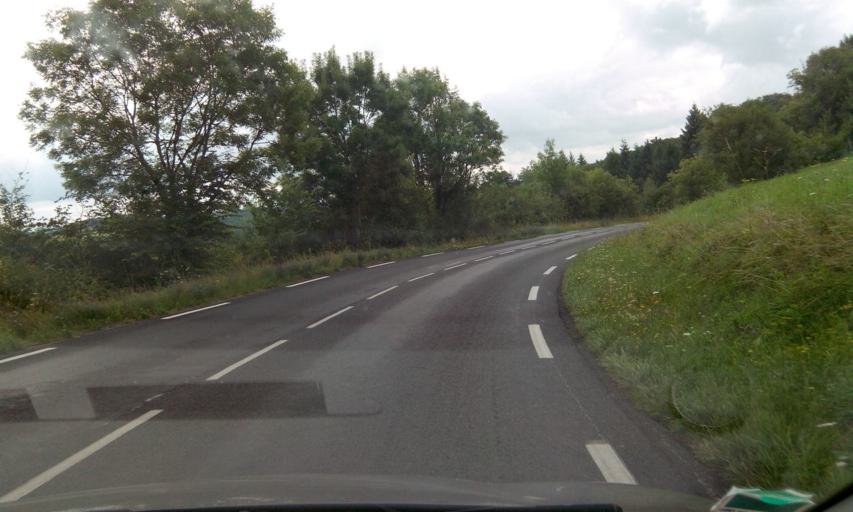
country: FR
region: Limousin
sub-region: Departement de la Correze
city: Cosnac
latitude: 45.0497
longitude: 1.5839
